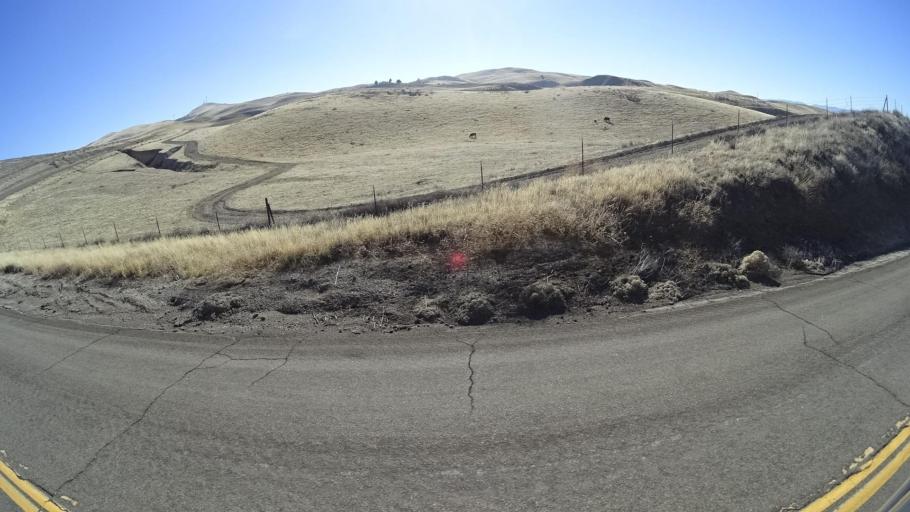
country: US
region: California
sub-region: Kern County
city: Maricopa
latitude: 34.9466
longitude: -119.4121
